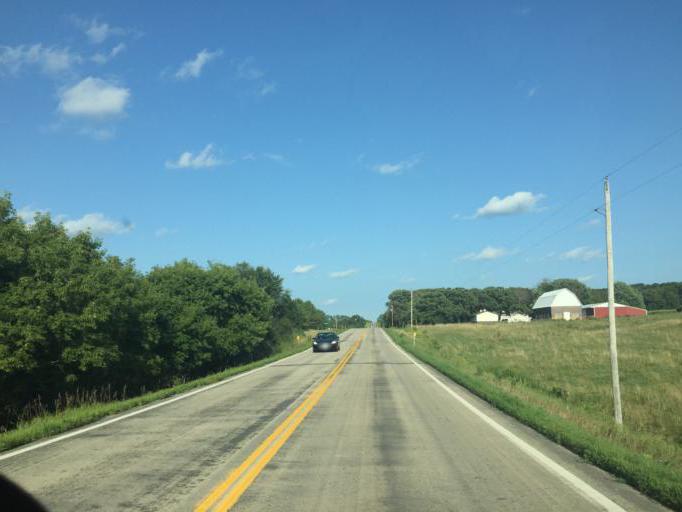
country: US
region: Minnesota
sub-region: Olmsted County
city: Rochester
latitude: 43.9640
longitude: -92.5472
